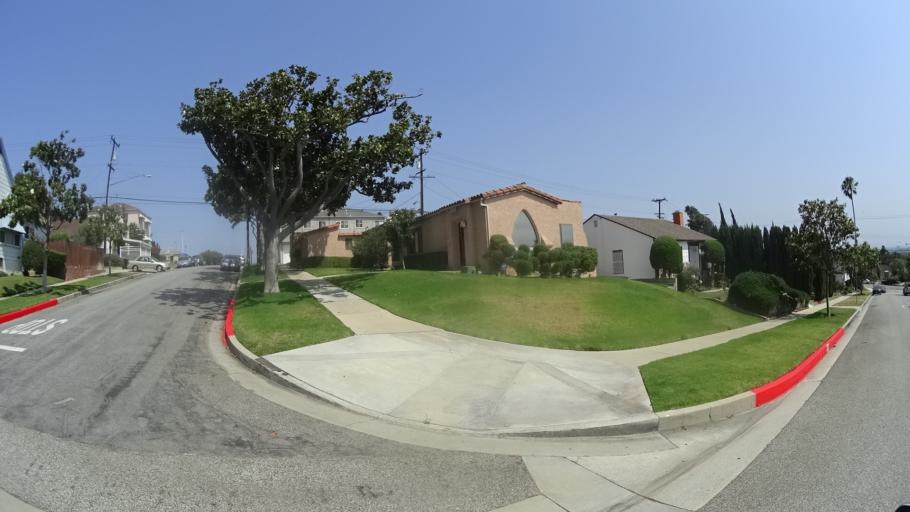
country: US
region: California
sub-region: Los Angeles County
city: View Park-Windsor Hills
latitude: 33.9846
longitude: -118.3560
